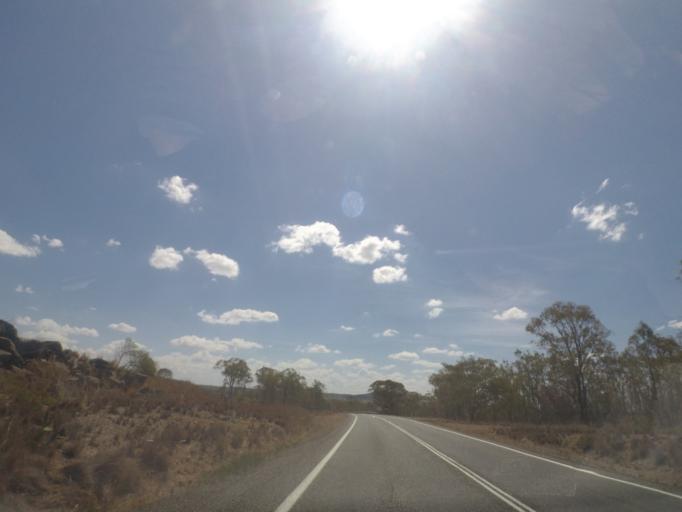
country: AU
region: Queensland
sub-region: Southern Downs
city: Warwick
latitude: -28.2053
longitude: 151.5743
